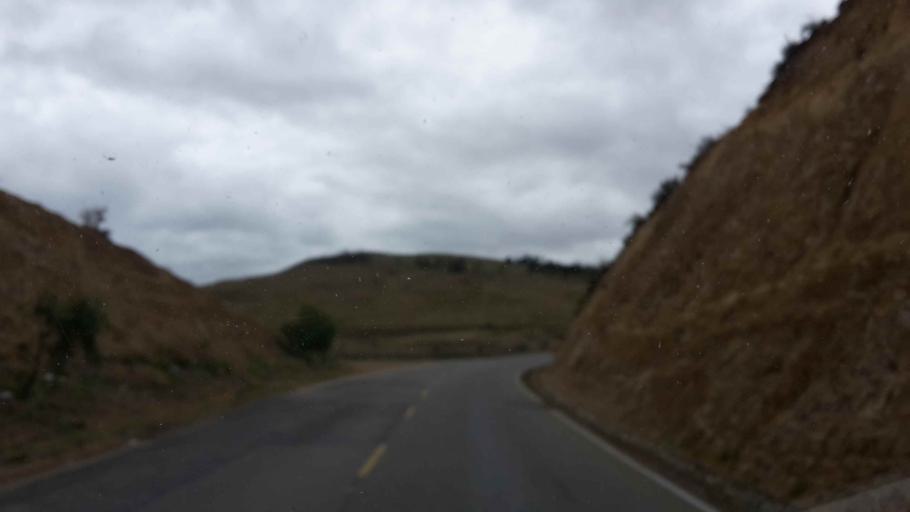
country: BO
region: Cochabamba
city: Punata
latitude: -17.4901
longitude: -65.7876
